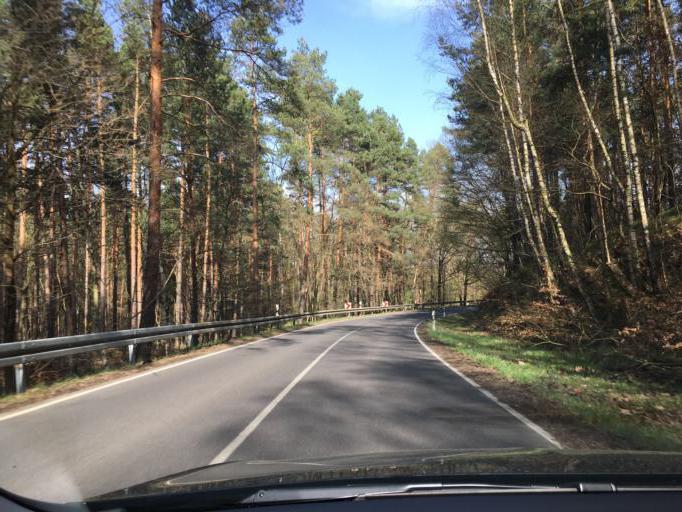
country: PL
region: Lubusz
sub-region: Powiat zarski
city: Leknica
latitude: 51.5201
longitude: 14.7478
